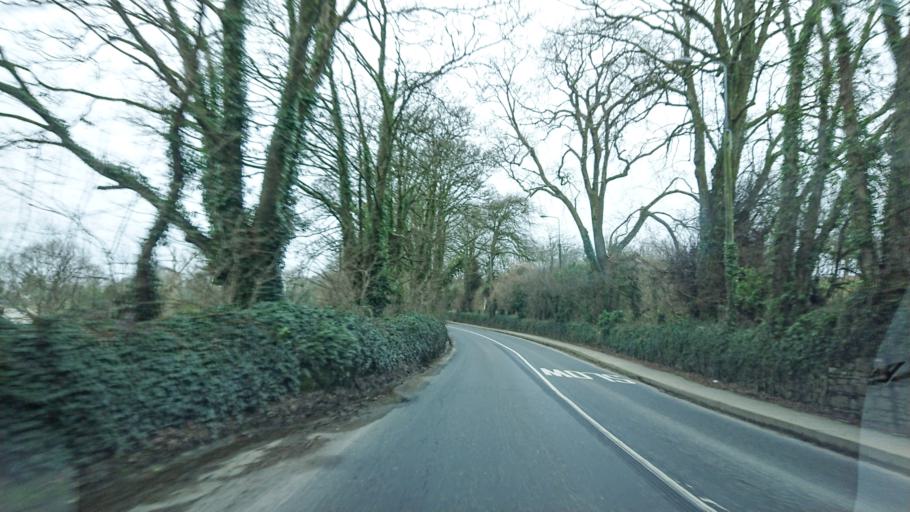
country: IE
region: Munster
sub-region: County Cork
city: Bandon
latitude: 51.7477
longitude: -8.7462
